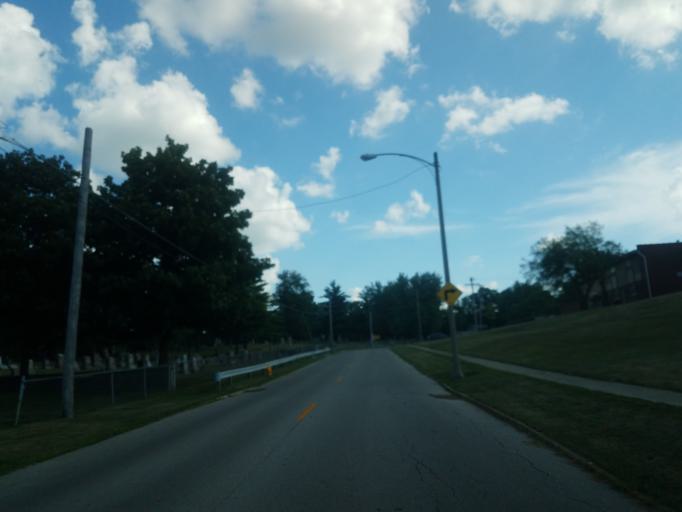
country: US
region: Illinois
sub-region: McLean County
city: Bloomington
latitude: 40.4722
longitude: -88.9898
